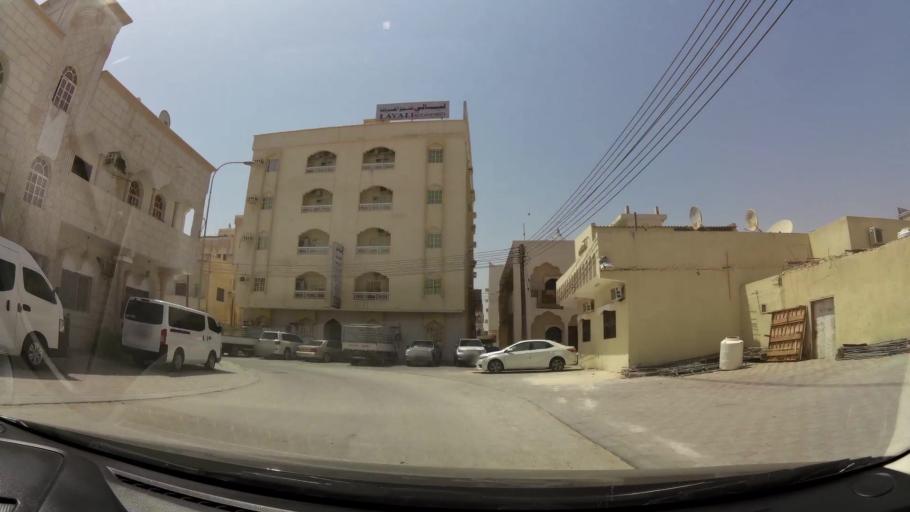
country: OM
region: Zufar
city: Salalah
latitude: 17.0167
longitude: 54.0844
